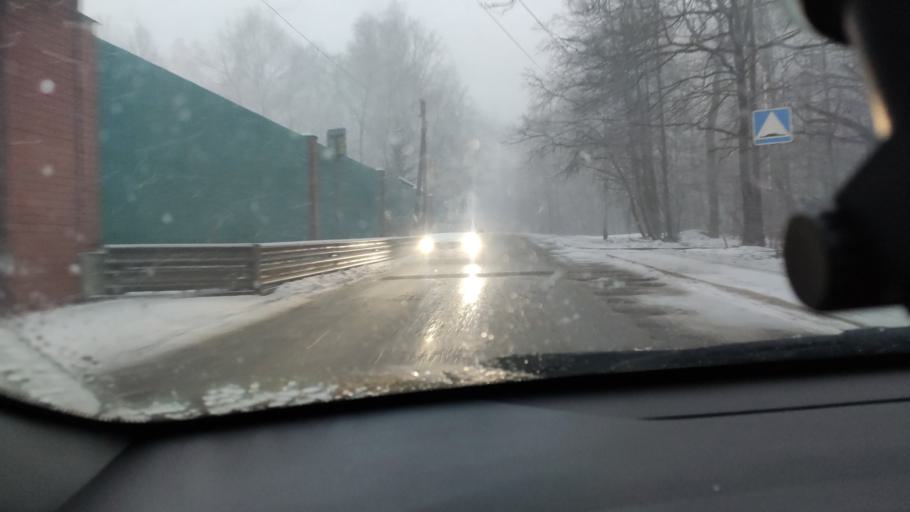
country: RU
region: Moskovskaya
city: Biryulevo Zapadnoye
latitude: 55.5531
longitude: 37.6269
